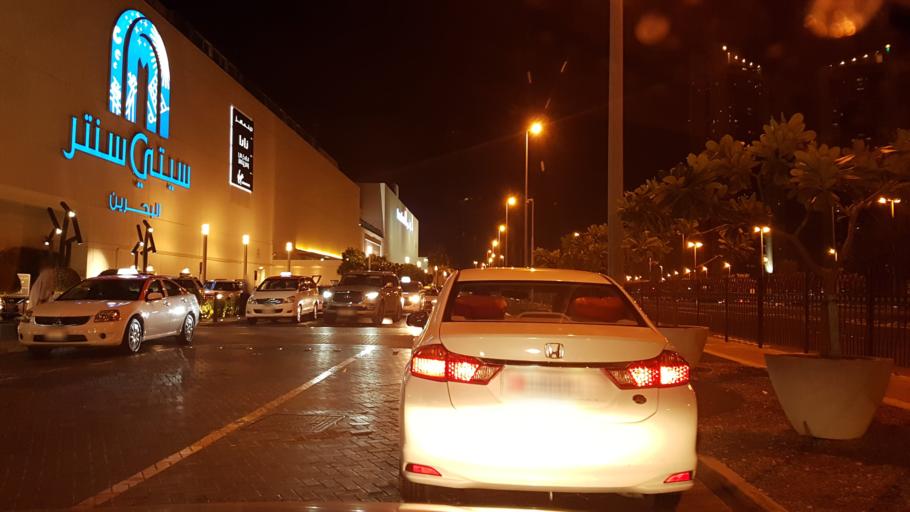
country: BH
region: Manama
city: Jidd Hafs
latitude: 26.2323
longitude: 50.5535
